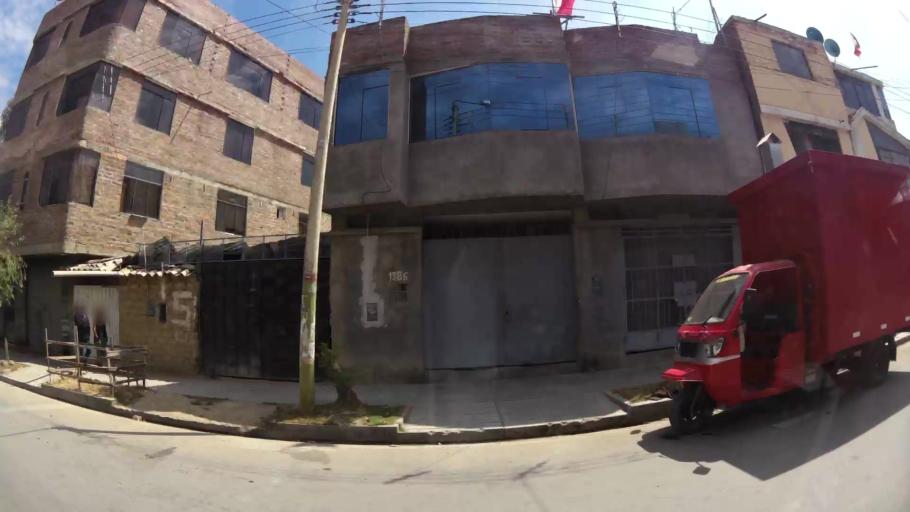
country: PE
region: Junin
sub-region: Provincia de Huancayo
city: El Tambo
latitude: -12.0757
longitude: -75.2164
